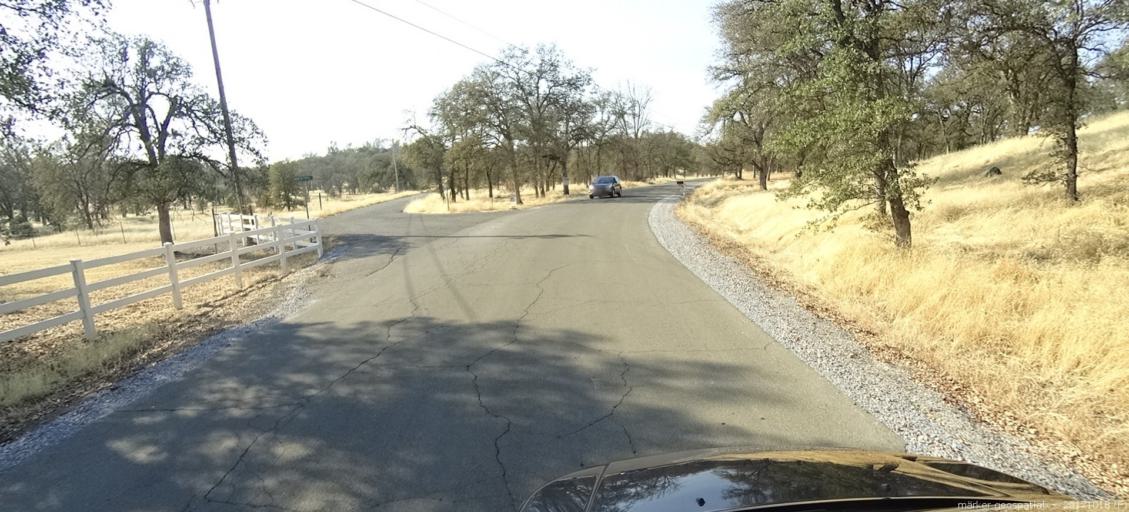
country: US
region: California
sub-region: Shasta County
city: Palo Cedro
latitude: 40.5710
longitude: -122.2478
